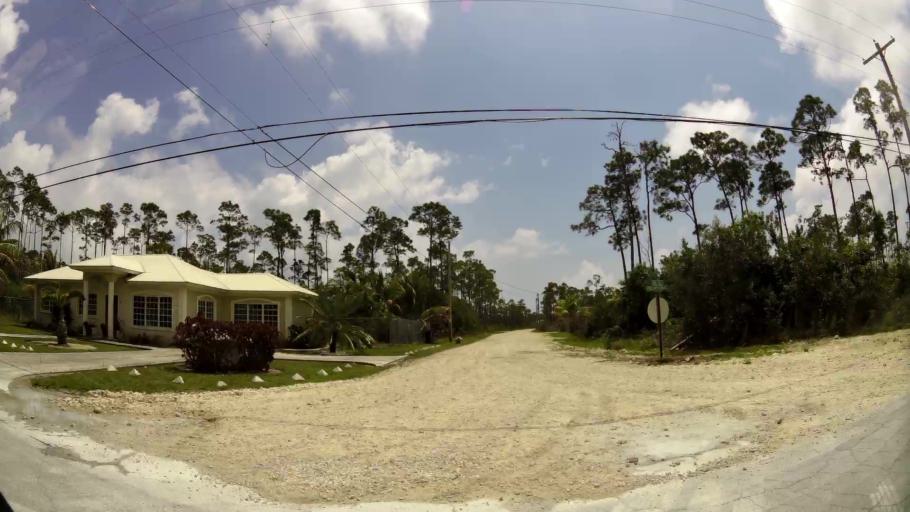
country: BS
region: Freeport
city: Lucaya
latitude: 26.5322
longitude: -78.6522
